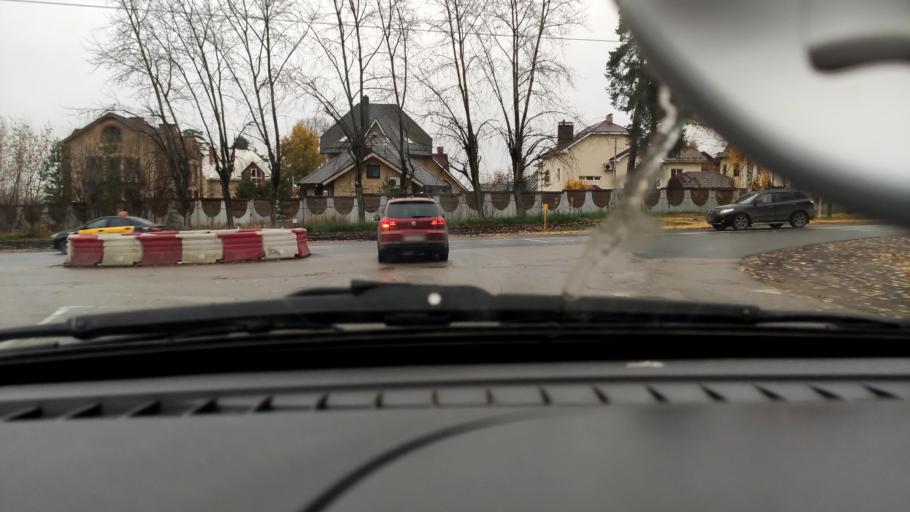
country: RU
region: Perm
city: Kondratovo
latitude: 58.0130
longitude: 55.9847
